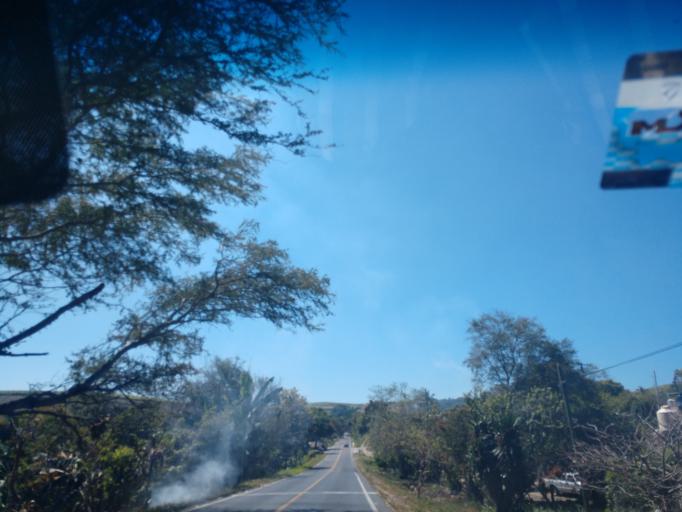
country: MX
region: Nayarit
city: Xalisco
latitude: 21.3820
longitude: -104.8902
